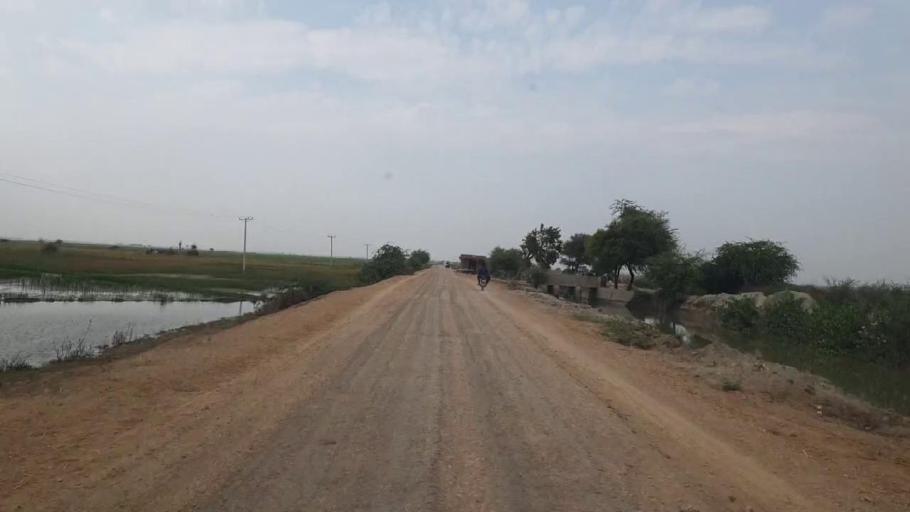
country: PK
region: Sindh
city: Kario
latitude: 24.6097
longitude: 68.5934
